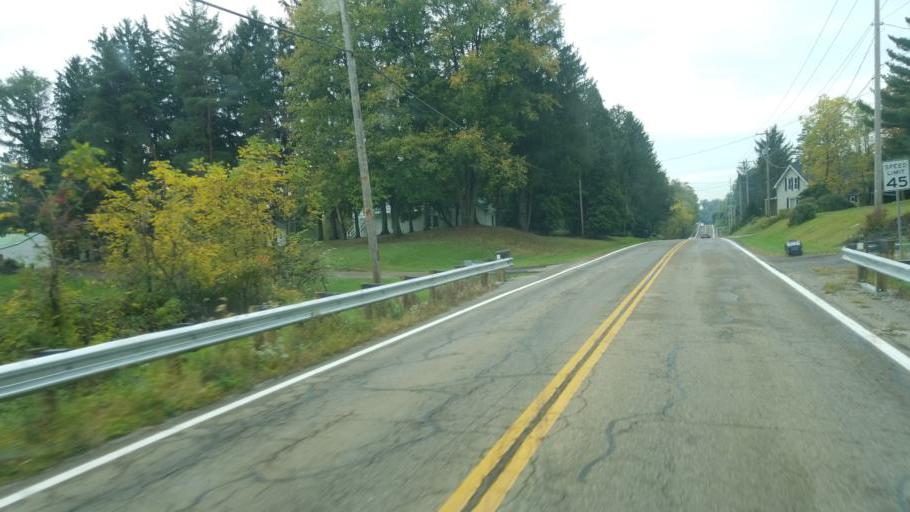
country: US
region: Ohio
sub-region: Knox County
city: Mount Vernon
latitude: 40.4189
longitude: -82.4621
